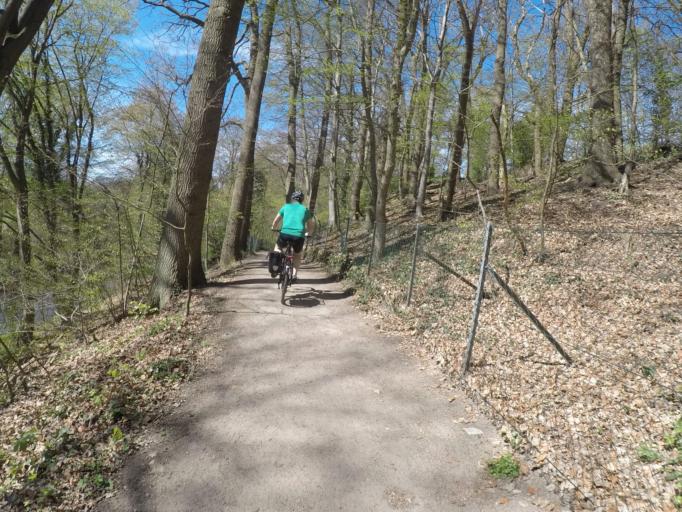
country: DE
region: Hamburg
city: Poppenbuettel
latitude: 53.6713
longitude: 10.0985
